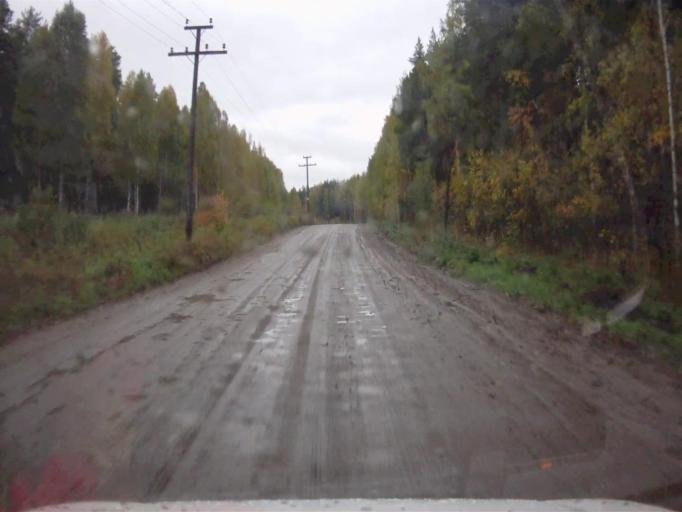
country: RU
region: Chelyabinsk
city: Kyshtym
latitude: 55.8023
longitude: 60.4798
